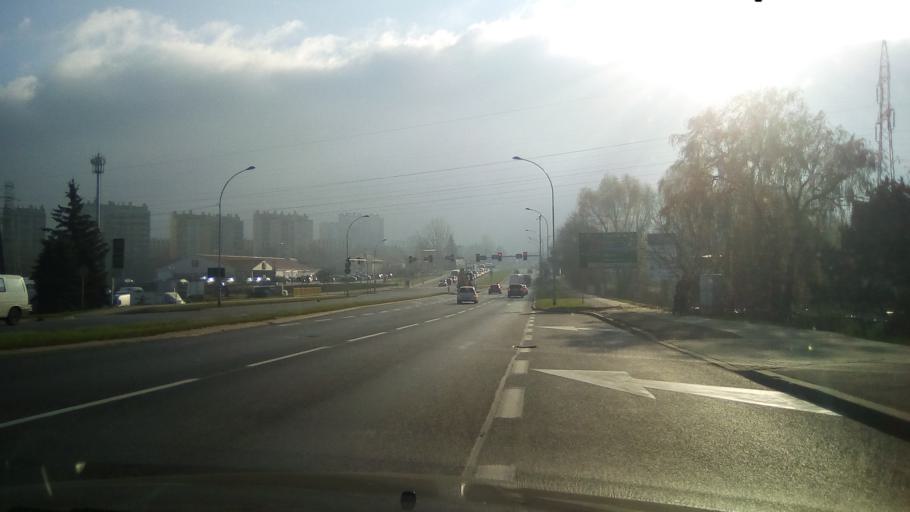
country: PL
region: Subcarpathian Voivodeship
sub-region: Rzeszow
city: Rzeszow
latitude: 50.0546
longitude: 21.9682
